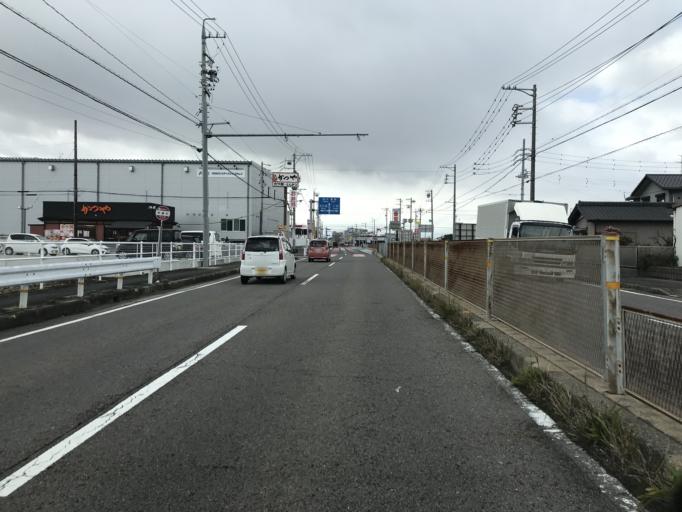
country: JP
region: Aichi
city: Iwakura
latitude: 35.2419
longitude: 136.8854
